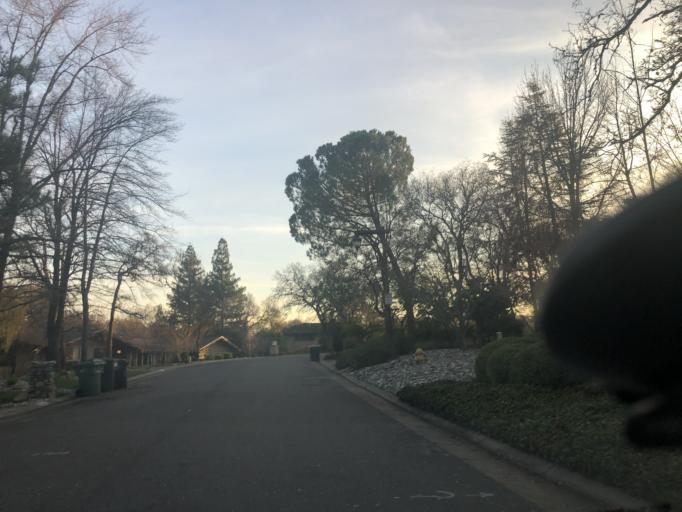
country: US
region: California
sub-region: Sacramento County
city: Gold River
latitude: 38.6399
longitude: -121.2293
